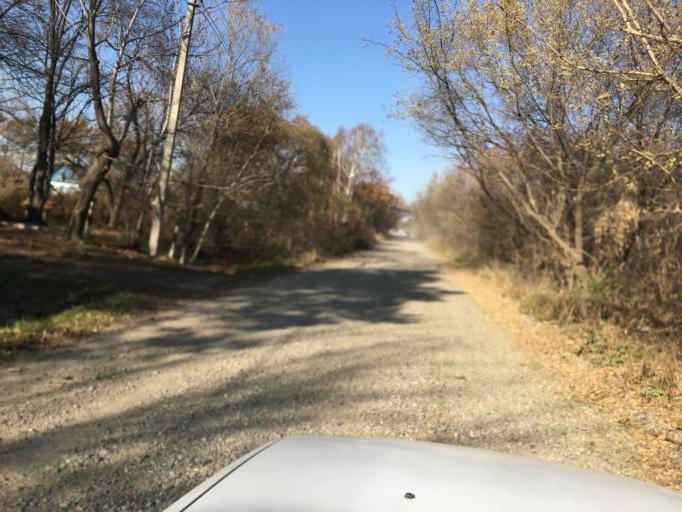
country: RU
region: Primorskiy
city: Dal'nerechensk
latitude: 45.9165
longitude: 133.7153
